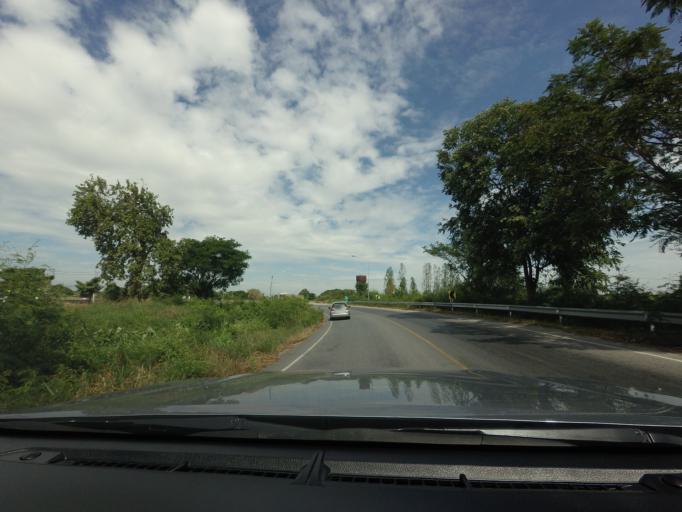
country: TH
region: Suphan Buri
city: Suphan Buri
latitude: 14.4645
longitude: 100.0912
